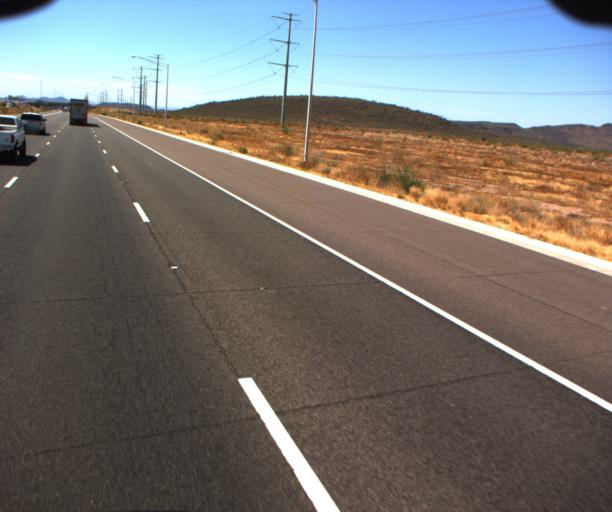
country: US
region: Arizona
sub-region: Maricopa County
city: Anthem
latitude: 33.7643
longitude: -112.1286
